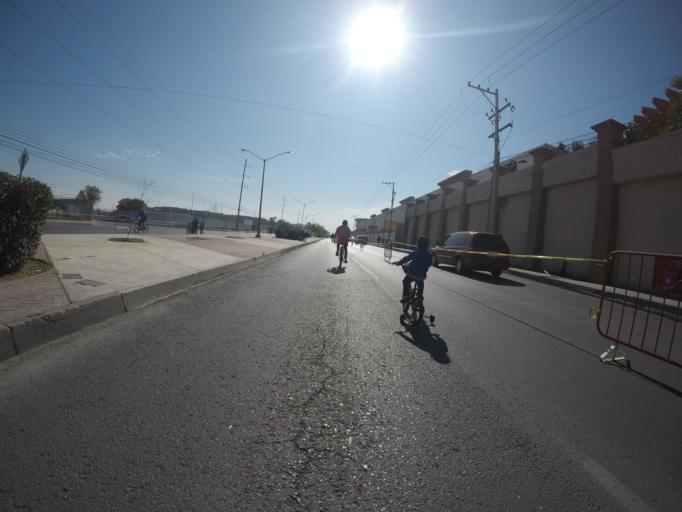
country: MX
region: Chihuahua
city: Ciudad Juarez
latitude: 31.7231
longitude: -106.4002
